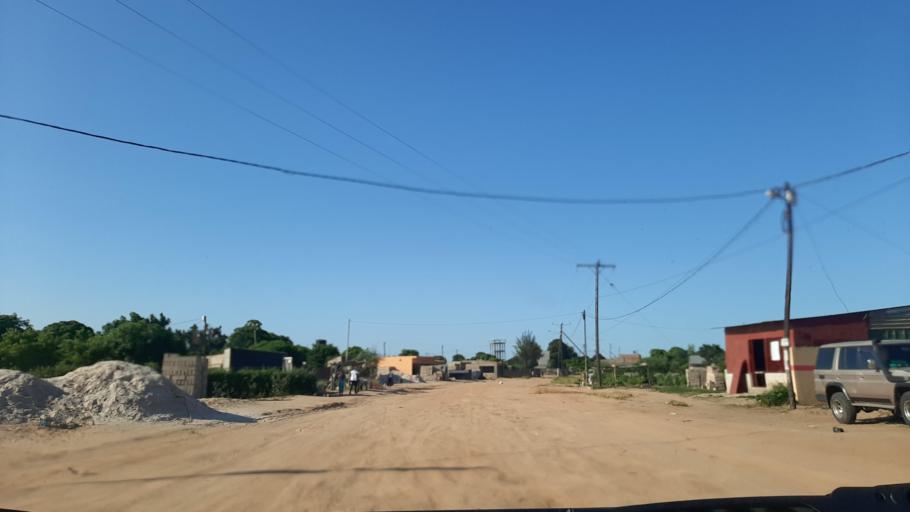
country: MZ
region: Maputo City
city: Maputo
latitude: -25.8035
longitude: 32.5472
